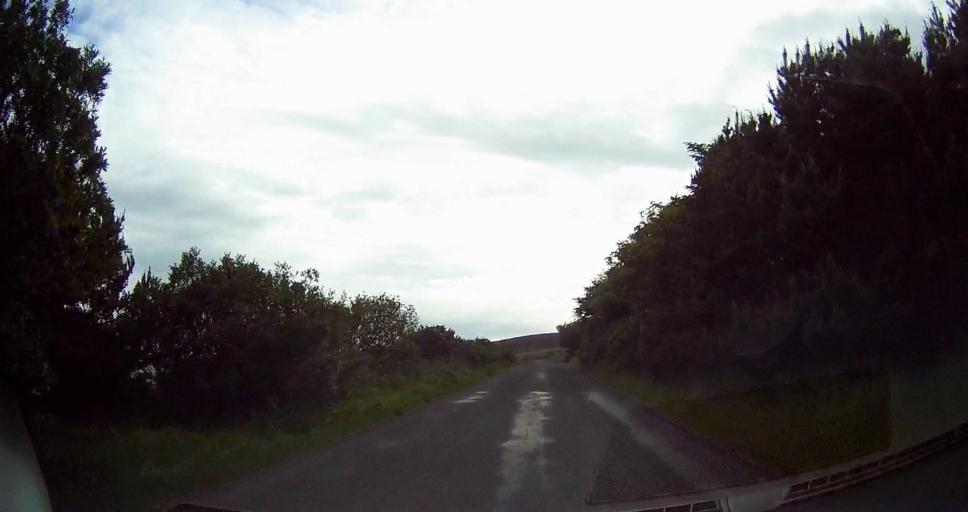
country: GB
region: Scotland
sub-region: Orkney Islands
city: Stromness
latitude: 58.8028
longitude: -3.2415
